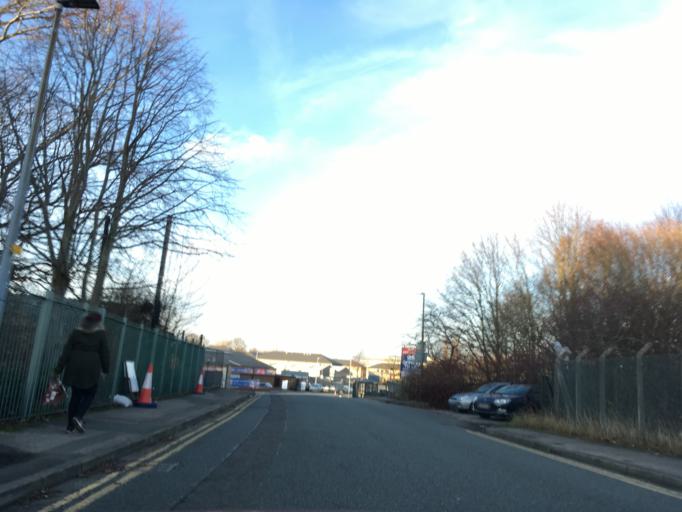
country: GB
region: England
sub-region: Borough of Stockport
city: Cheadle Hulme
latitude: 53.3531
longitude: -2.2053
